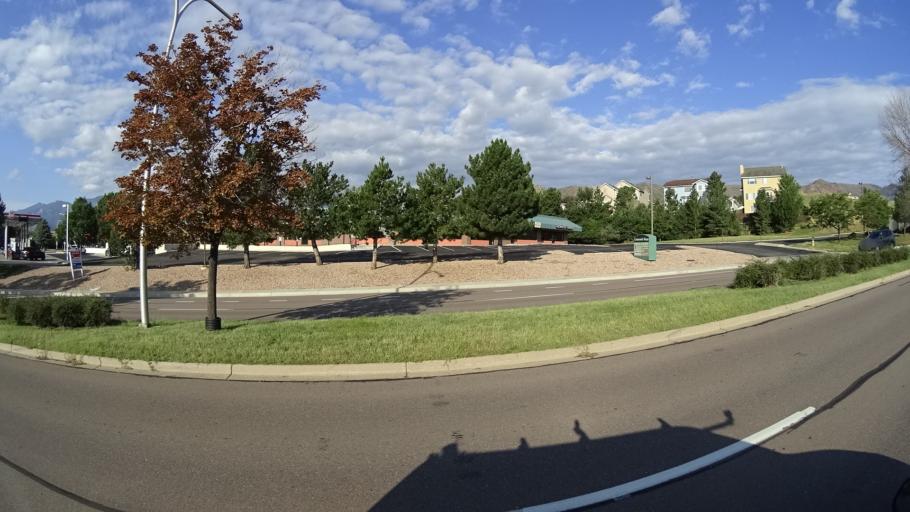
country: US
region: Colorado
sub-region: El Paso County
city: Manitou Springs
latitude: 38.9052
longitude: -104.8632
